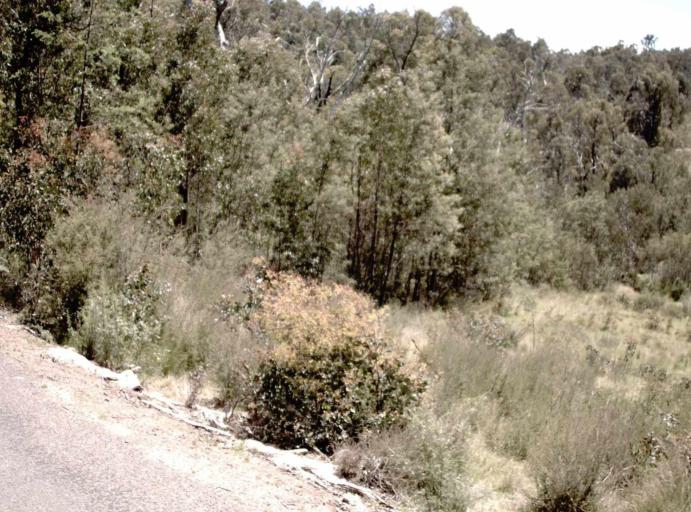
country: AU
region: New South Wales
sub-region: Snowy River
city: Jindabyne
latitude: -37.1156
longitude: 148.2436
